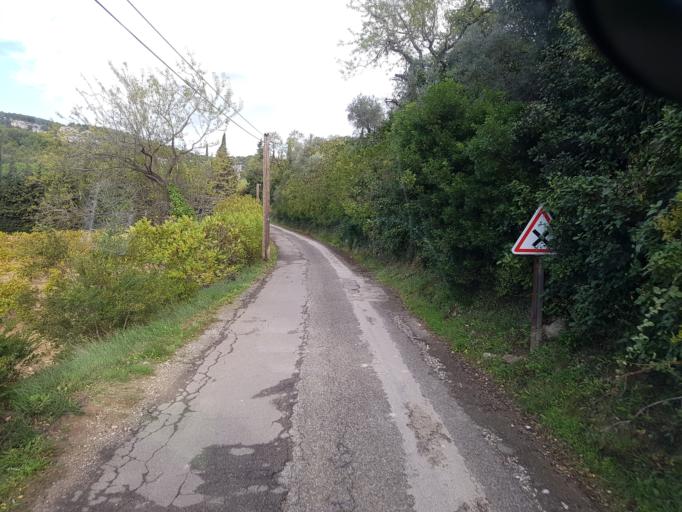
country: FR
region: Provence-Alpes-Cote d'Azur
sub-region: Departement des Bouches-du-Rhone
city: Cassis
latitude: 43.2245
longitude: 5.5603
